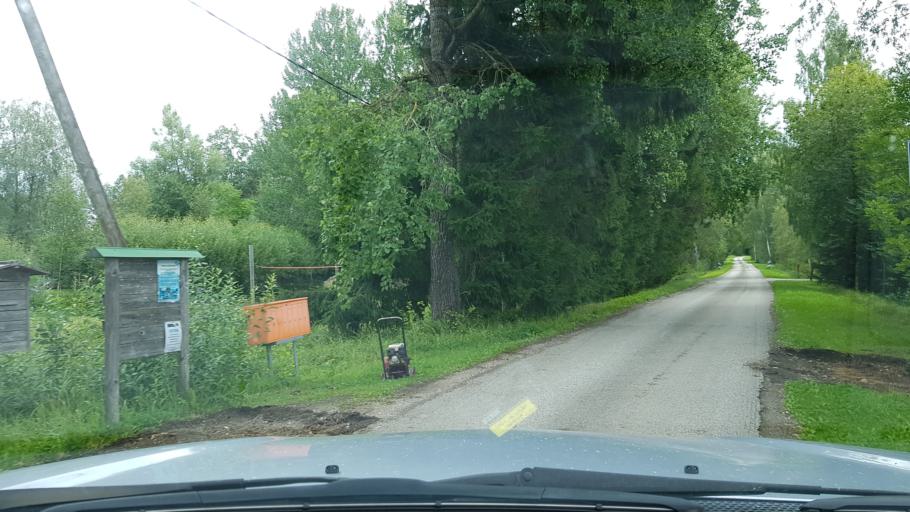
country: EE
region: Harju
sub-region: Raasiku vald
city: Arukula
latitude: 59.2916
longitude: 25.0661
